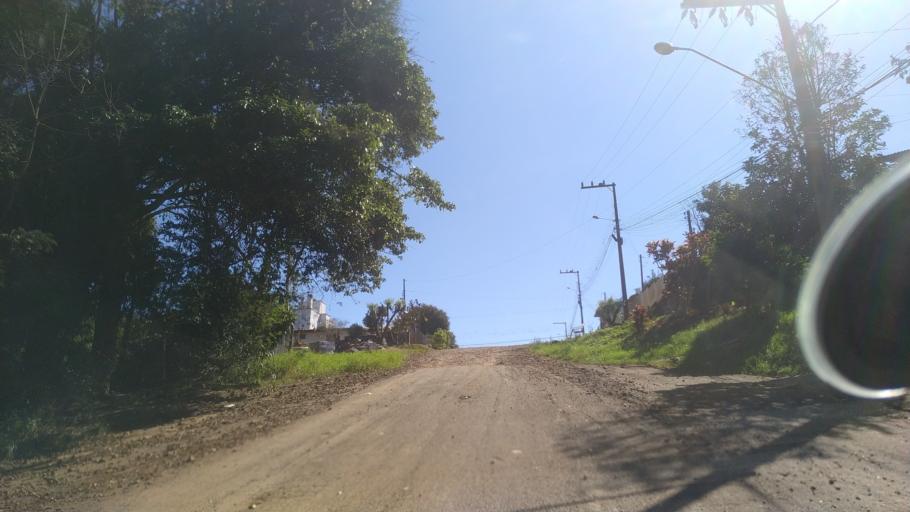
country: BR
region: Santa Catarina
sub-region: Chapeco
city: Chapeco
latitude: -27.1211
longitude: -52.5939
